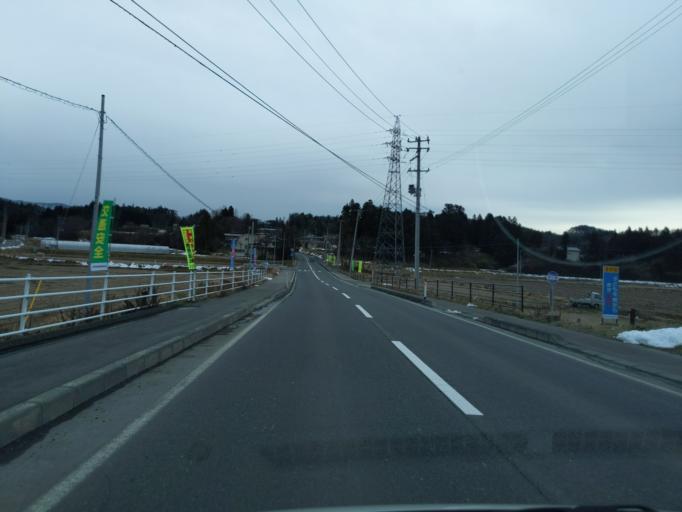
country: JP
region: Iwate
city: Mizusawa
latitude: 39.1592
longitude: 141.2036
